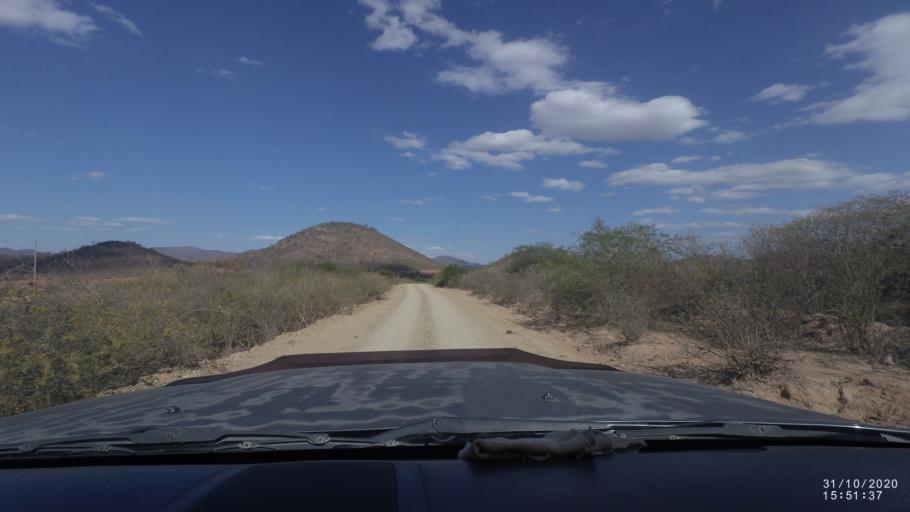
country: BO
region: Chuquisaca
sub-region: Provincia Zudanez
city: Mojocoya
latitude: -18.3164
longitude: -64.7014
